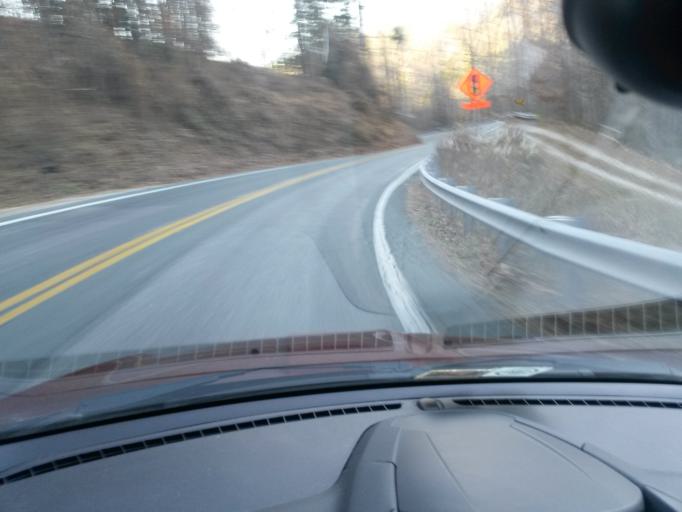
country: US
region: Virginia
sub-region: City of Buena Vista
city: Buena Vista
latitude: 37.7434
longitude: -79.2597
